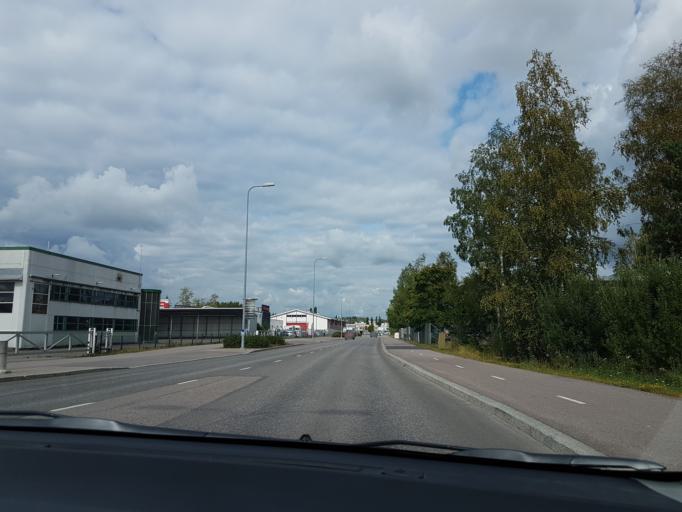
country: FI
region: Uusimaa
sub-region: Helsinki
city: Jaervenpaeae
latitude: 60.4725
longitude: 25.1158
